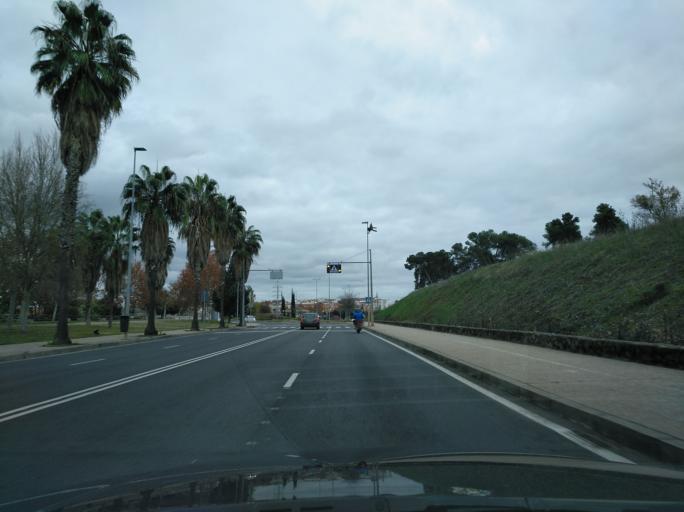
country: ES
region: Extremadura
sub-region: Provincia de Badajoz
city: Badajoz
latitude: 38.8836
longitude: -6.9660
